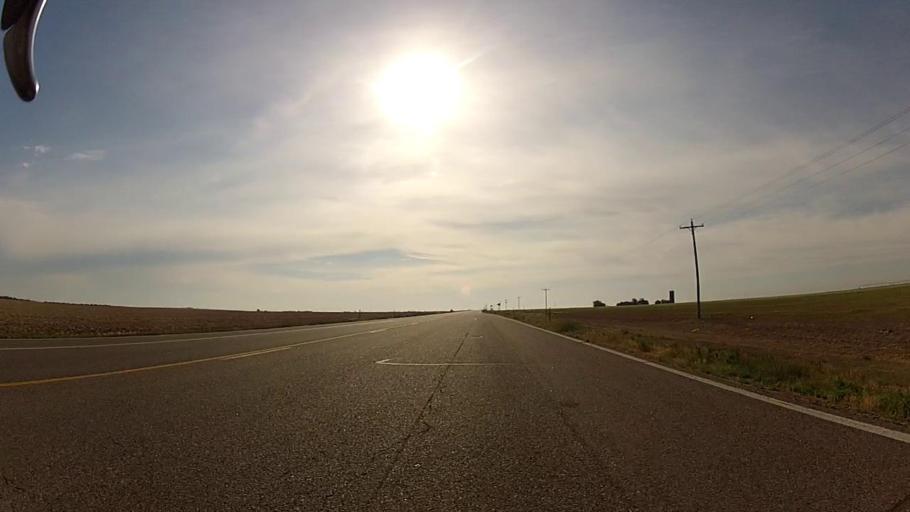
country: US
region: Kansas
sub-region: Grant County
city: Ulysses
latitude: 37.5766
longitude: -101.4528
